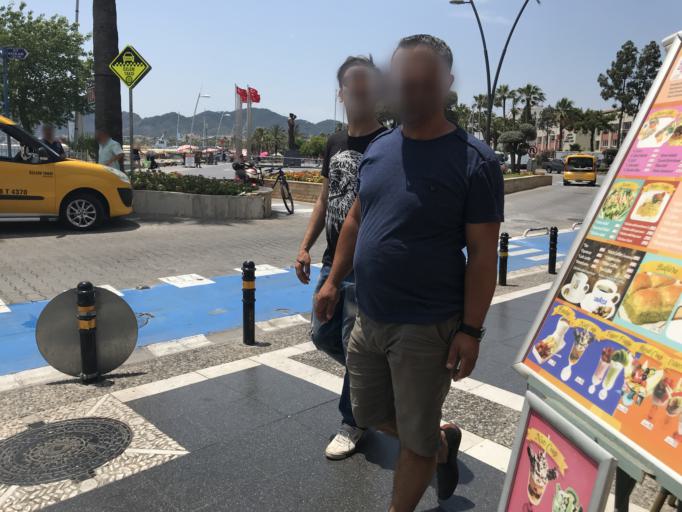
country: TR
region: Mugla
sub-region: Marmaris
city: Marmaris
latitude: 36.8531
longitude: 28.2716
